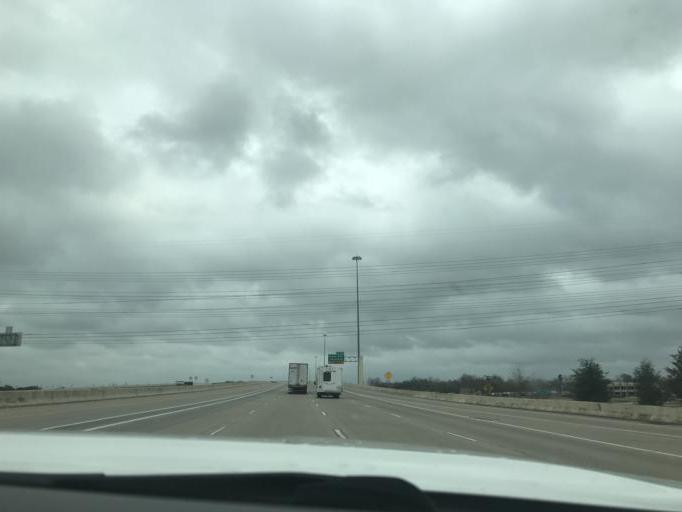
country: US
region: Texas
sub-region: Fort Bend County
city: Greatwood
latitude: 29.5606
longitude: -95.6939
